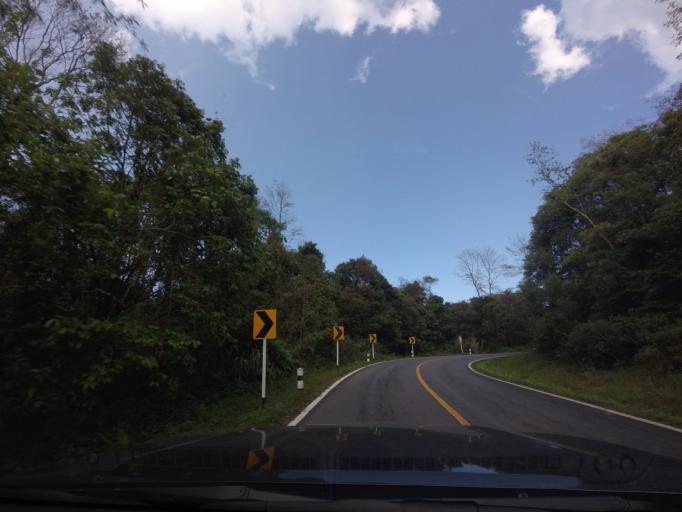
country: TH
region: Phetchabun
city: Lom Kao
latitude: 16.9492
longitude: 101.0285
